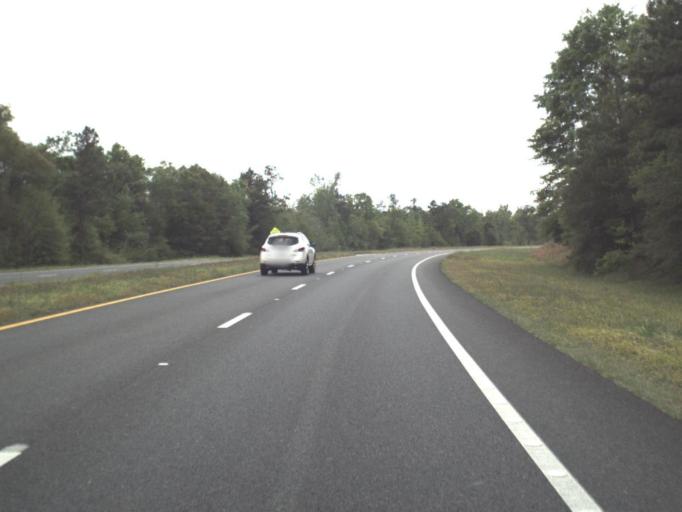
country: US
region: Florida
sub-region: Escambia County
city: Molino
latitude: 30.8492
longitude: -87.3220
